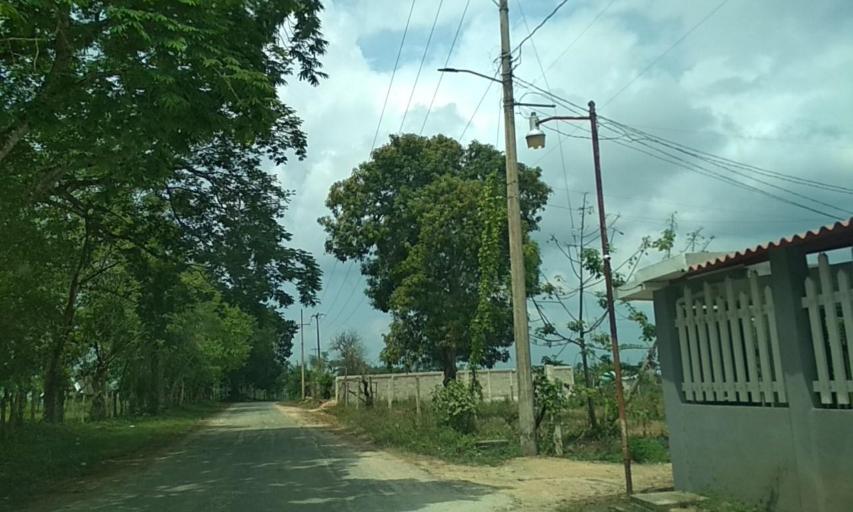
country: MX
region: Veracruz
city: Las Choapas
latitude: 17.8892
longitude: -94.1093
